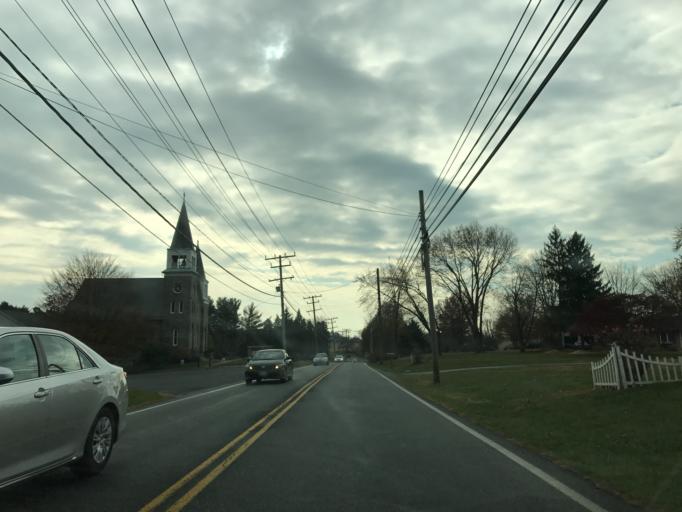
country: US
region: Maryland
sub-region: Harford County
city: Jarrettsville
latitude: 39.6027
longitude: -76.4415
